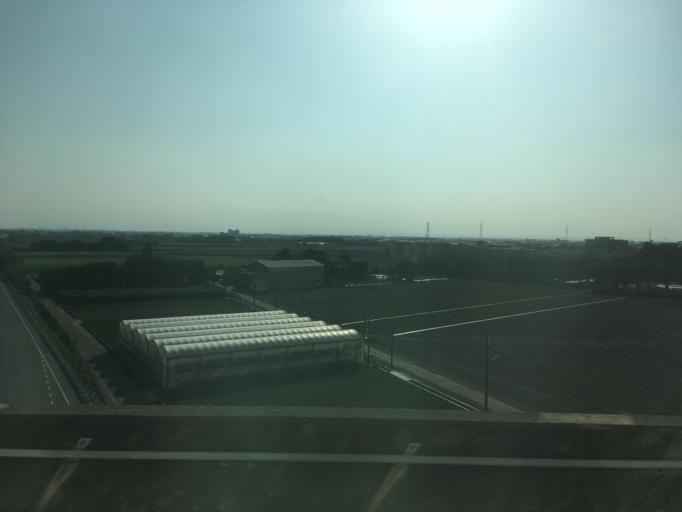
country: TW
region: Taiwan
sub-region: Yunlin
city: Douliu
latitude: 23.6900
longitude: 120.3887
